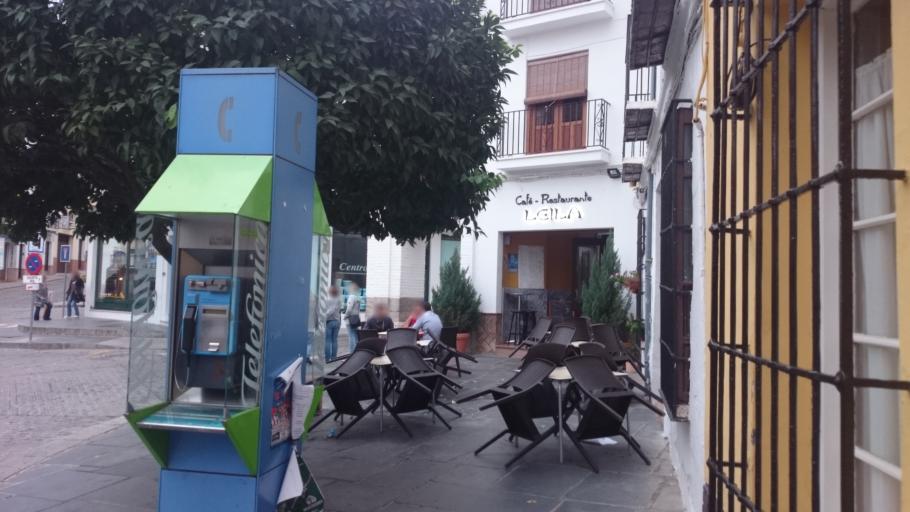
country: ES
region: Andalusia
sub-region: Provincia de Malaga
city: Antequera
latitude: 37.0162
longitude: -4.5595
